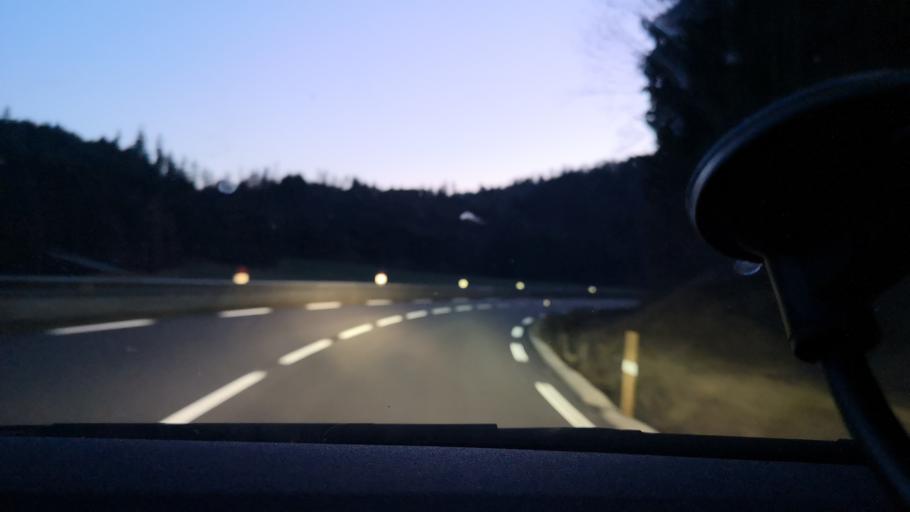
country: FR
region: Franche-Comte
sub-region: Departement du Jura
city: Champagnole
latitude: 46.7569
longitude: 5.9767
